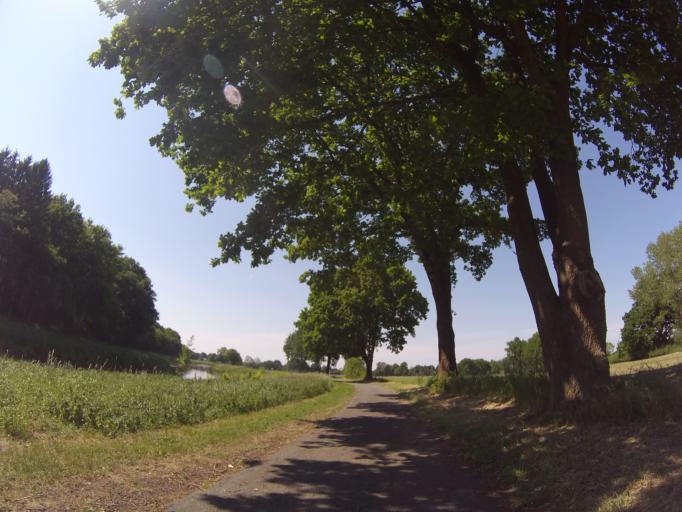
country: DE
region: Lower Saxony
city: Emlichheim
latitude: 52.6010
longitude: 6.8454
